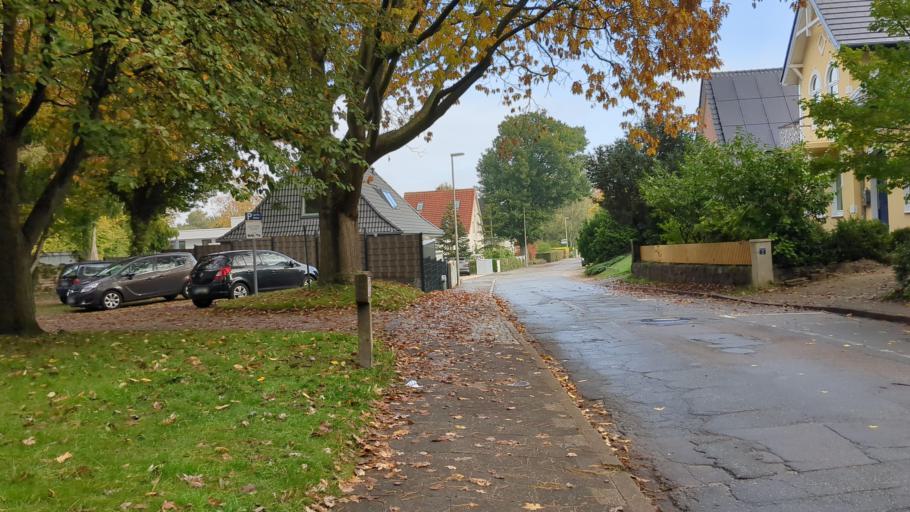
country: DE
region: Schleswig-Holstein
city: Wees
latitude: 54.8172
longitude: 9.4731
